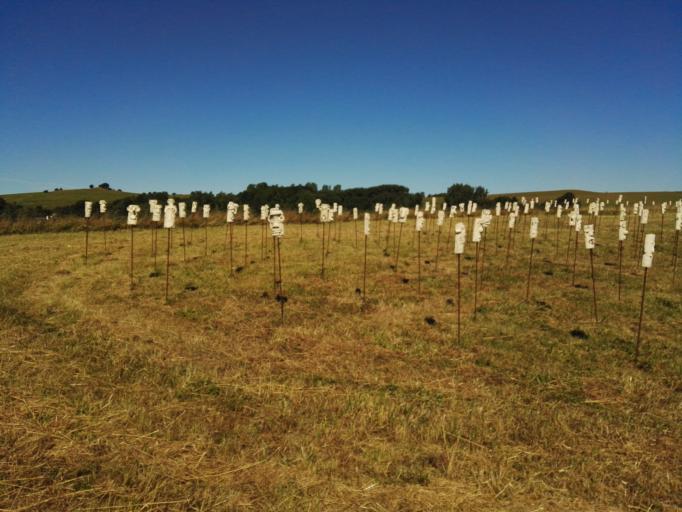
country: DK
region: Zealand
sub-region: Odsherred Kommune
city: Asnaes
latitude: 55.8267
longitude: 11.4608
